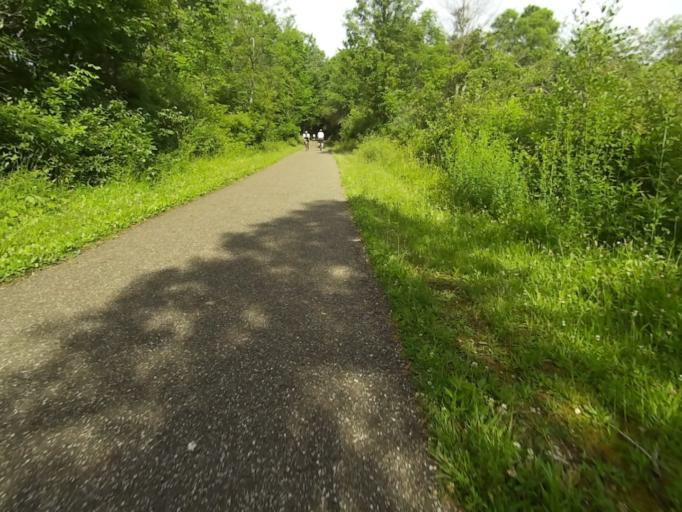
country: US
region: Ohio
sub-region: Summit County
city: Stow
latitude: 41.1903
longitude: -81.3983
